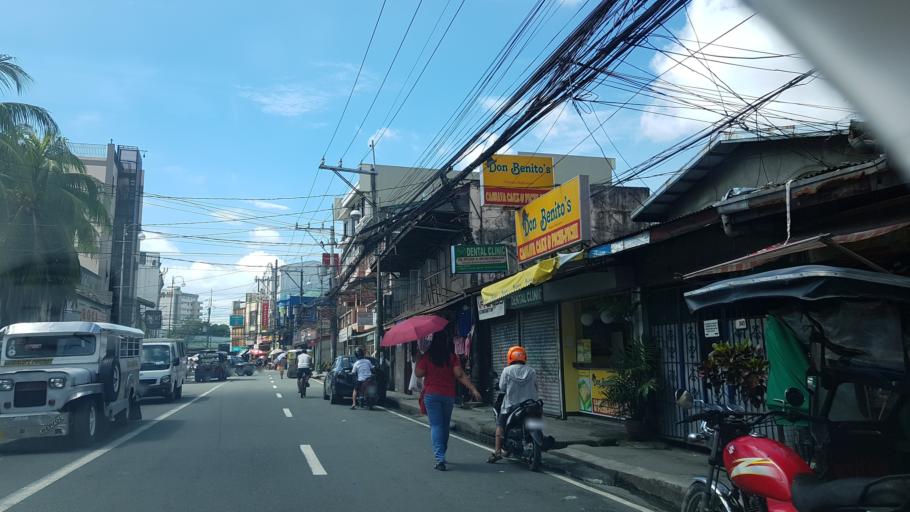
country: PH
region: Calabarzon
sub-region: Province of Rizal
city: Pateros
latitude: 14.5475
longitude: 121.0641
